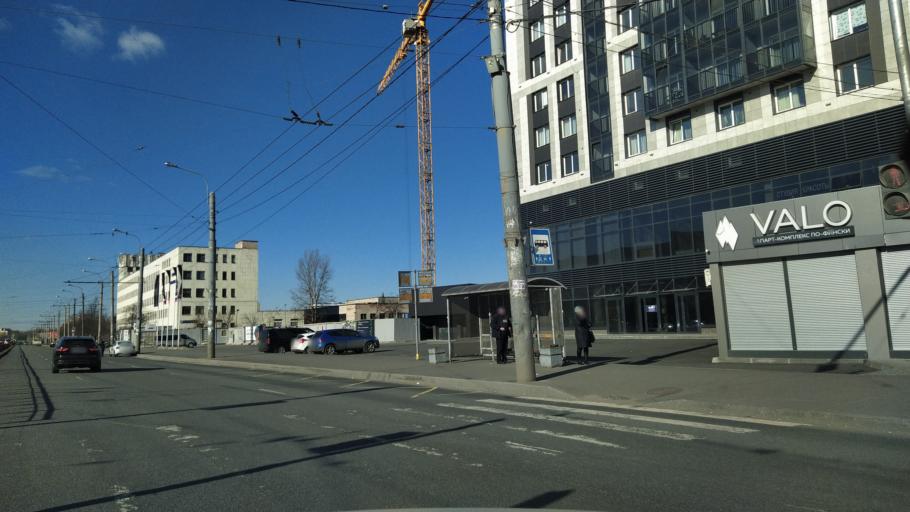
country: RU
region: St.-Petersburg
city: Kupchino
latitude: 59.8842
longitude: 30.3670
